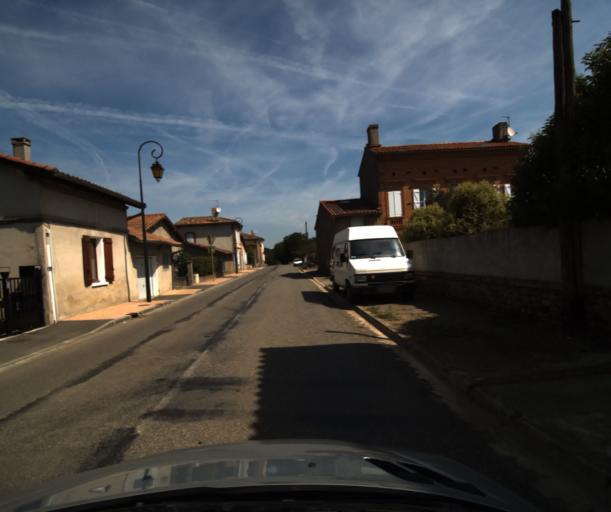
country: FR
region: Midi-Pyrenees
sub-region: Departement de la Haute-Garonne
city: Labastidette
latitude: 43.4691
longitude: 1.2161
